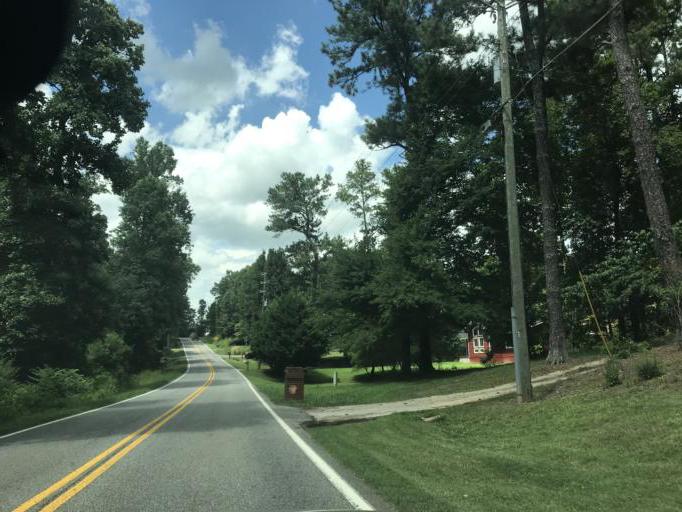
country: US
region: Georgia
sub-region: Forsyth County
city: Cumming
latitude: 34.1949
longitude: -84.1220
